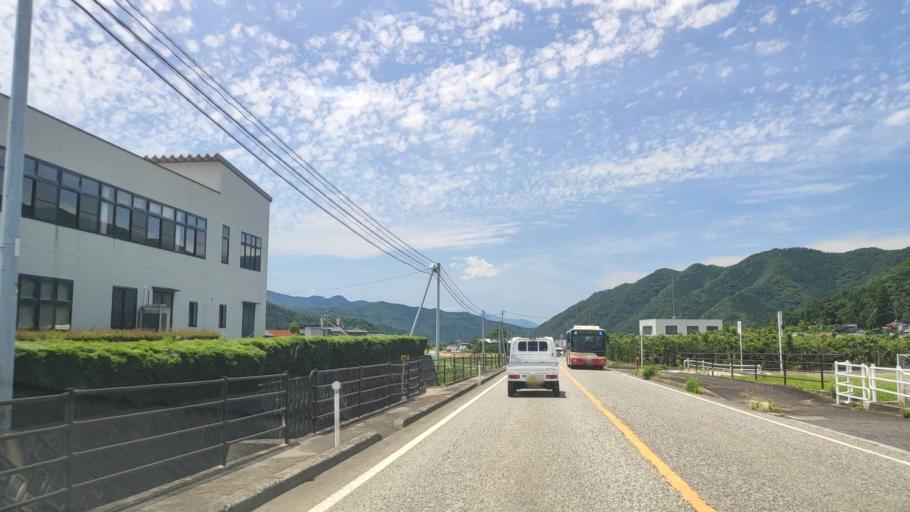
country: JP
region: Tottori
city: Tottori
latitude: 35.3621
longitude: 134.3519
